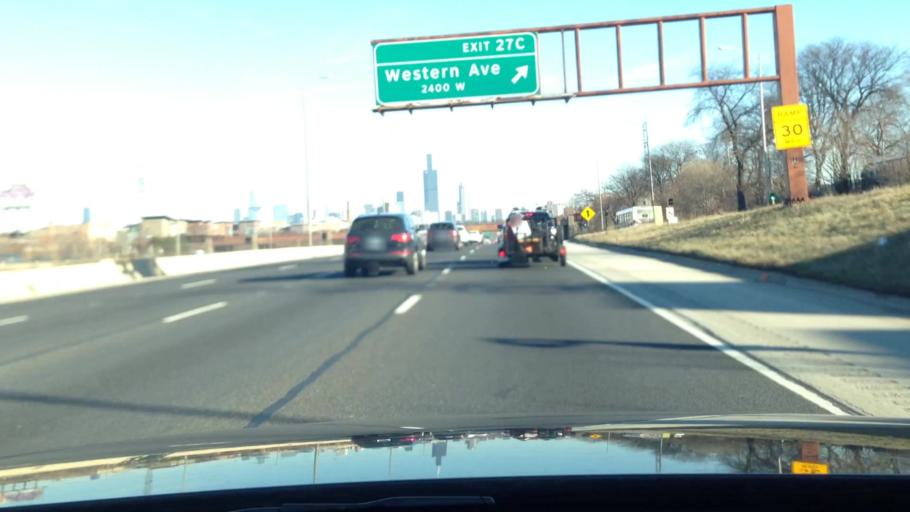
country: US
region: Illinois
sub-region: Cook County
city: Chicago
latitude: 41.8752
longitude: -87.6946
